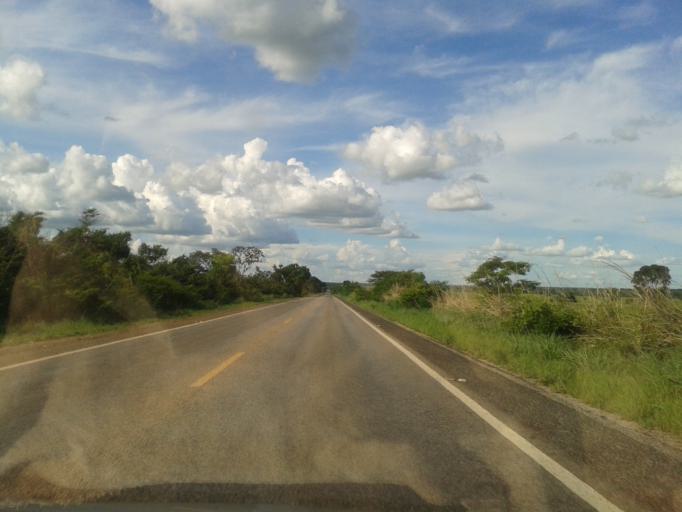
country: BR
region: Goias
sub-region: Mozarlandia
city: Mozarlandia
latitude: -14.5211
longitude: -50.4856
